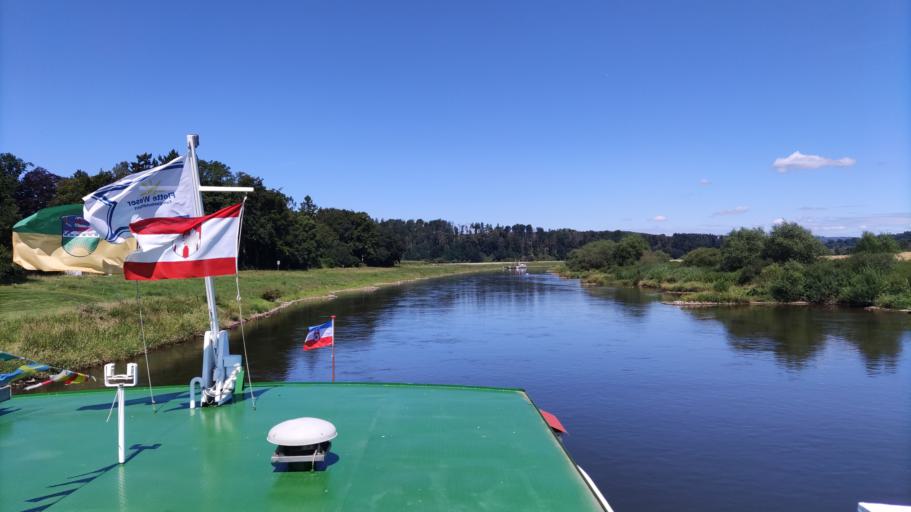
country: DE
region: Lower Saxony
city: Furstenberg
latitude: 51.7130
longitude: 9.3916
